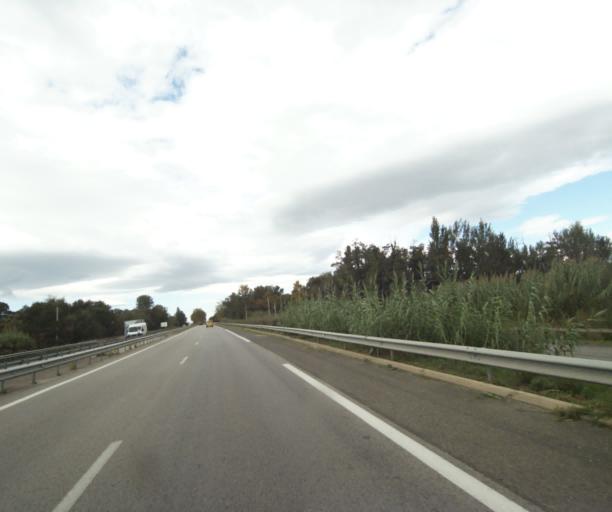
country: FR
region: Languedoc-Roussillon
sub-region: Departement des Pyrenees-Orientales
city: Latour-Bas-Elne
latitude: 42.5744
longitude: 2.9957
